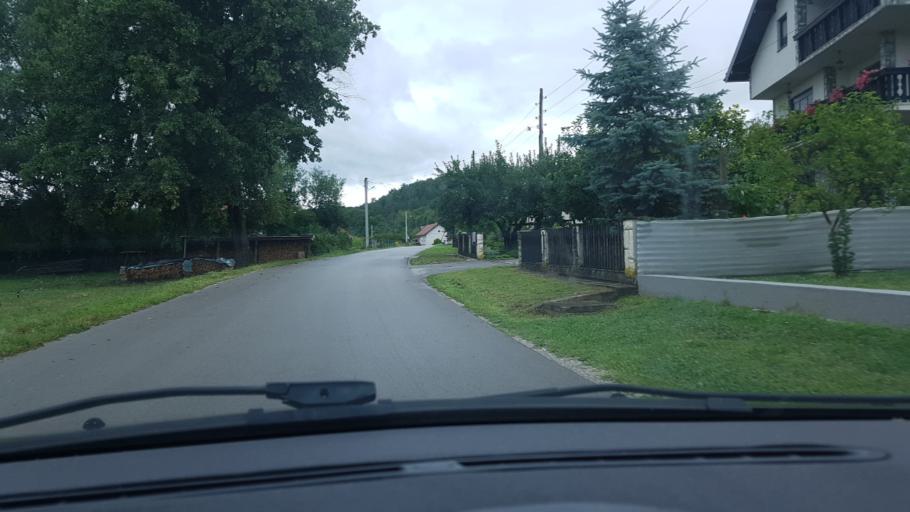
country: HR
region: Karlovacka
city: Ozalj
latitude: 45.5891
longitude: 15.5378
